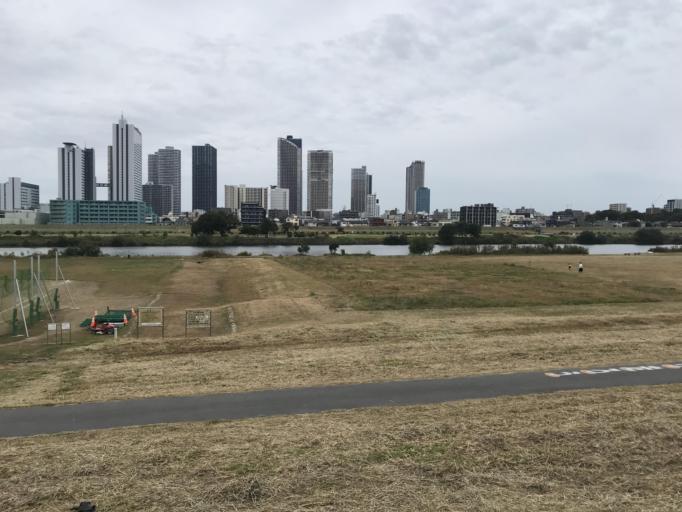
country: JP
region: Kanagawa
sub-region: Kawasaki-shi
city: Kawasaki
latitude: 35.5762
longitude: 139.6746
